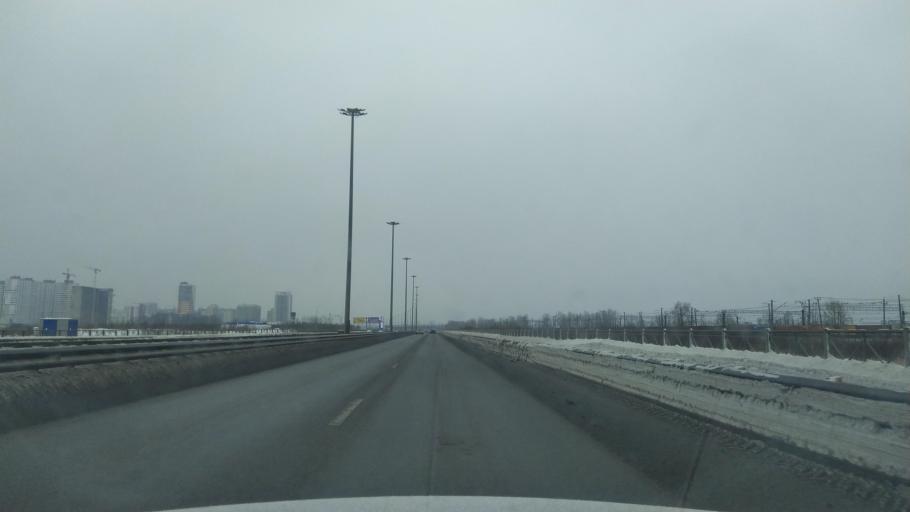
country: RU
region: St.-Petersburg
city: Shushary
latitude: 59.7942
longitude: 30.3927
